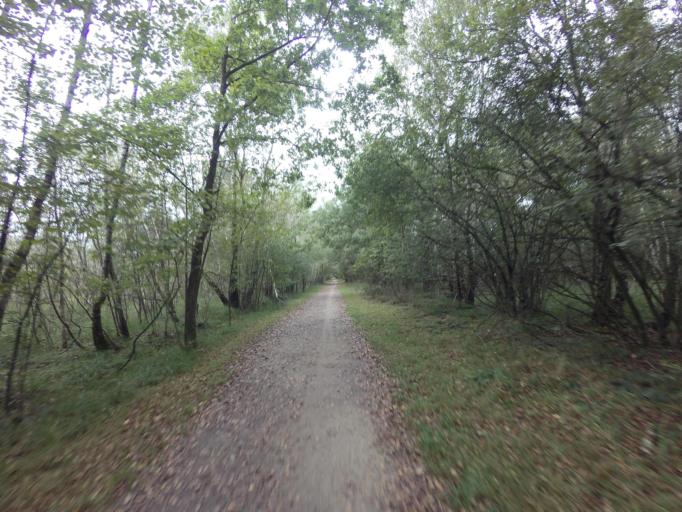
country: DE
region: North Rhine-Westphalia
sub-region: Regierungsbezirk Munster
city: Gronau
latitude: 52.2477
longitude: 7.0921
